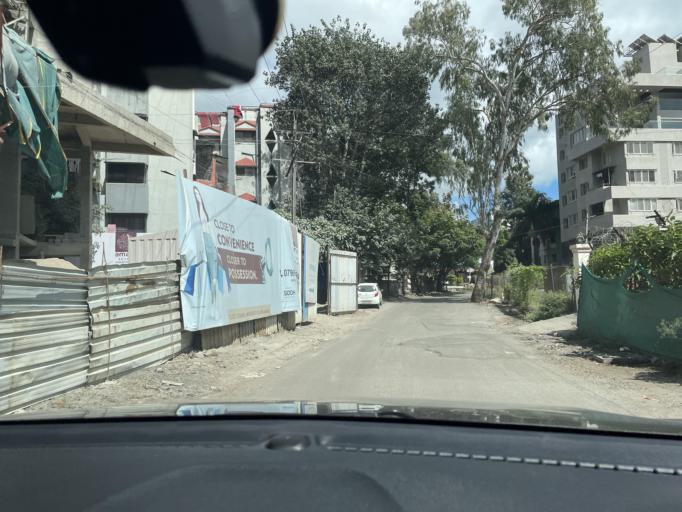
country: IN
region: Maharashtra
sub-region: Pune Division
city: Kharakvasla
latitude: 18.5154
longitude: 73.7781
